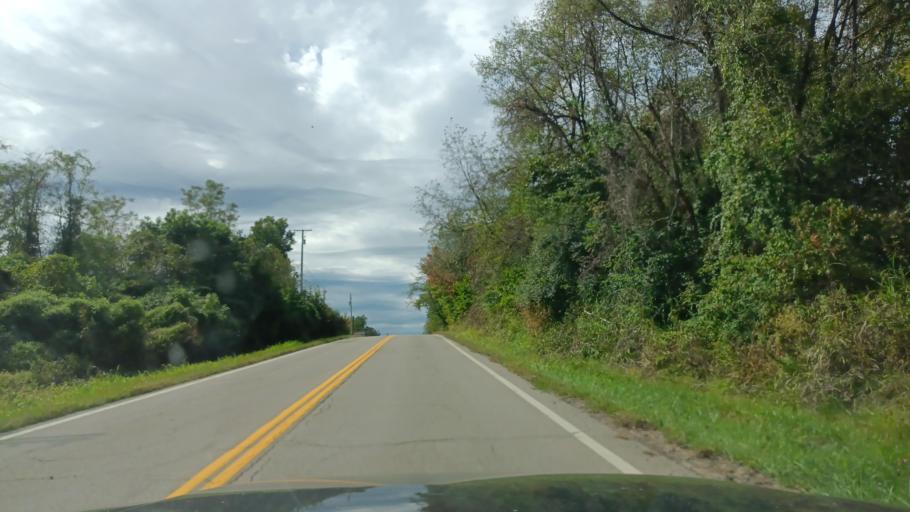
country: US
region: Ohio
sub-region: Athens County
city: Athens
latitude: 39.2120
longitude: -82.2404
